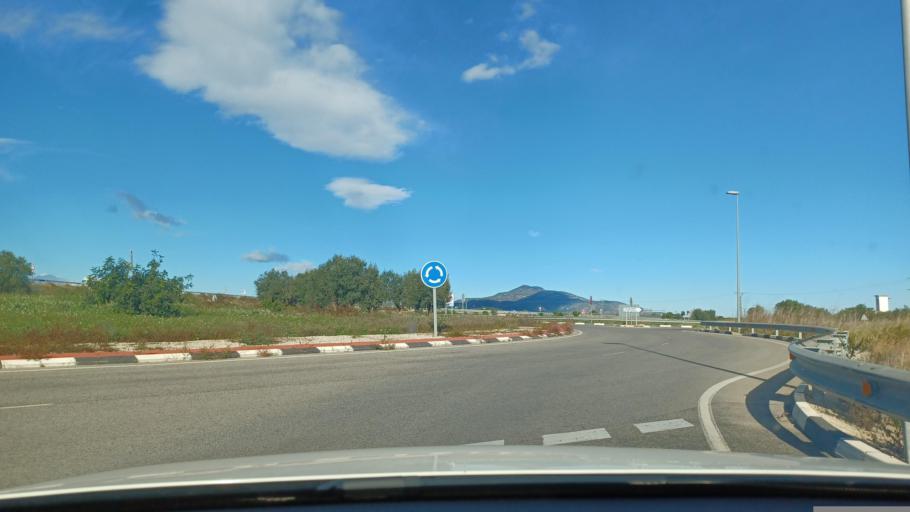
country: ES
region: Valencia
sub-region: Provincia de Castello
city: Vinaros
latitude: 40.4961
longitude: 0.4647
